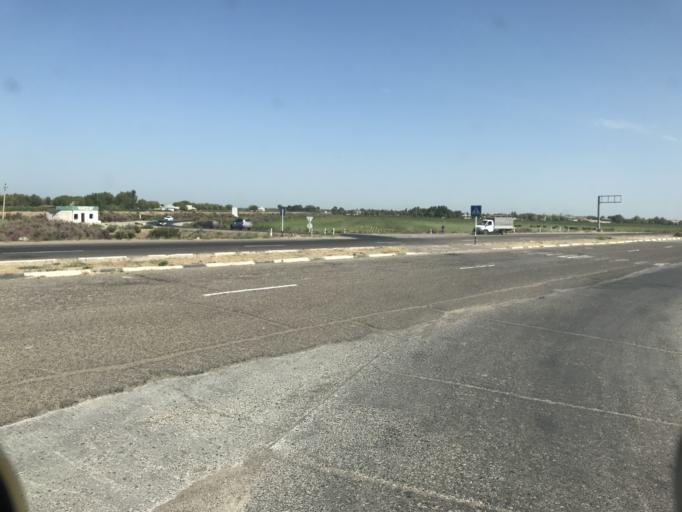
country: KZ
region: Ongtustik Qazaqstan
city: Myrzakent
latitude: 40.7487
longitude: 68.5376
